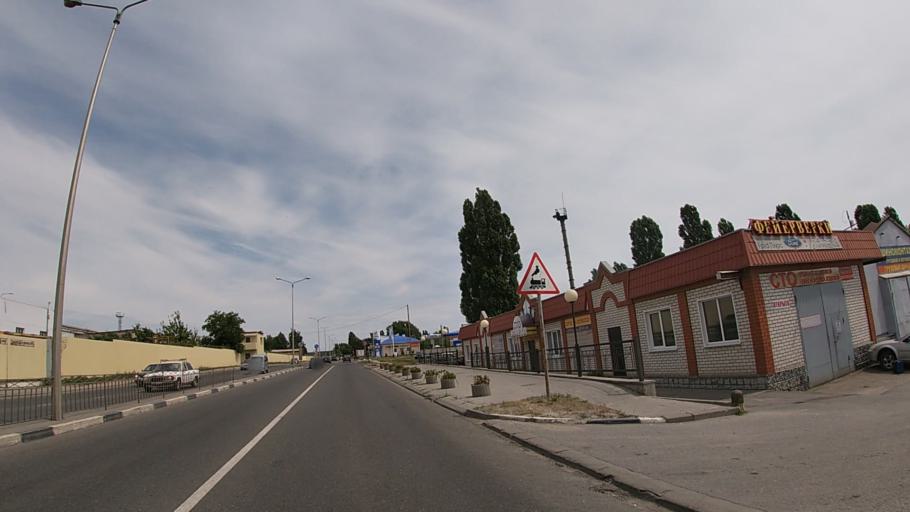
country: RU
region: Belgorod
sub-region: Belgorodskiy Rayon
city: Belgorod
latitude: 50.6150
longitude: 36.5371
